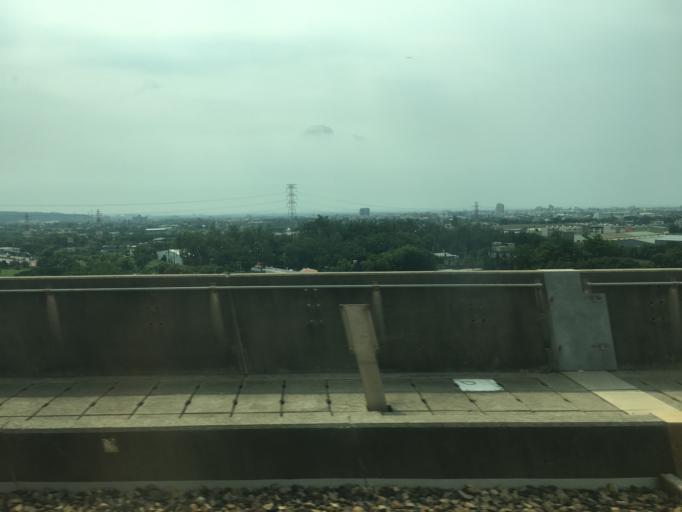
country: TW
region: Taiwan
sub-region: Hsinchu
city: Zhubei
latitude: 24.8800
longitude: 121.0683
